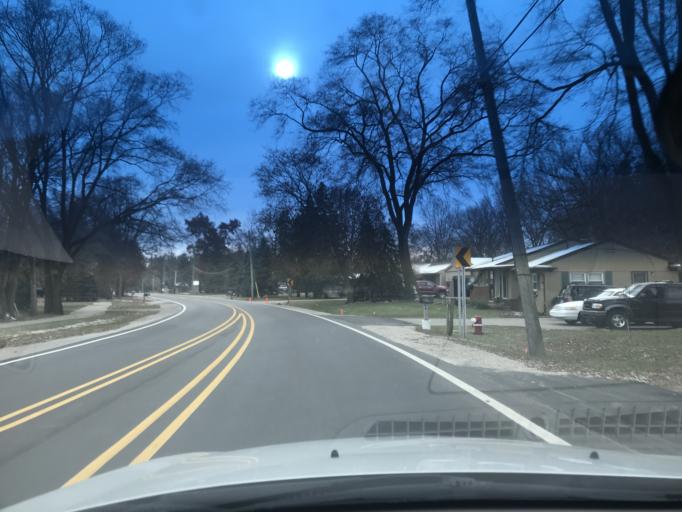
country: US
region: Michigan
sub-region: Macomb County
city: Shelby
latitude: 42.6678
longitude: -83.0632
